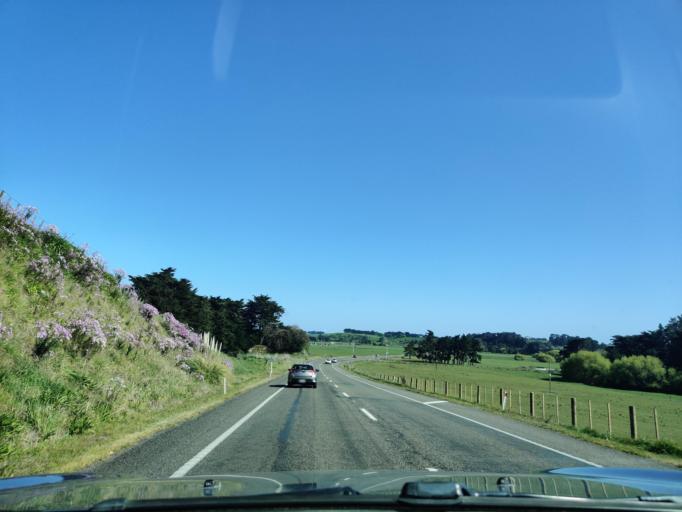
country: NZ
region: Manawatu-Wanganui
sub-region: Rangitikei District
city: Bulls
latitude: -40.0718
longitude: 175.2306
